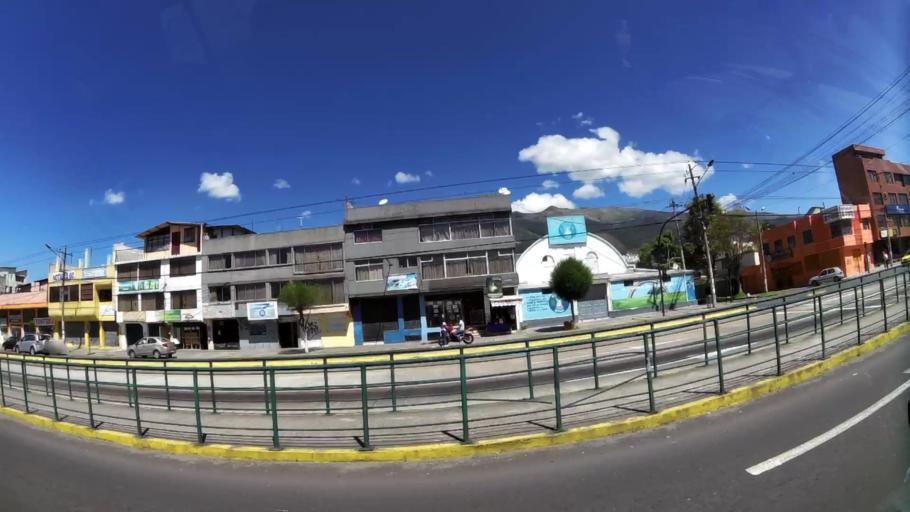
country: EC
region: Pichincha
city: Quito
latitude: -0.1526
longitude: -78.4896
